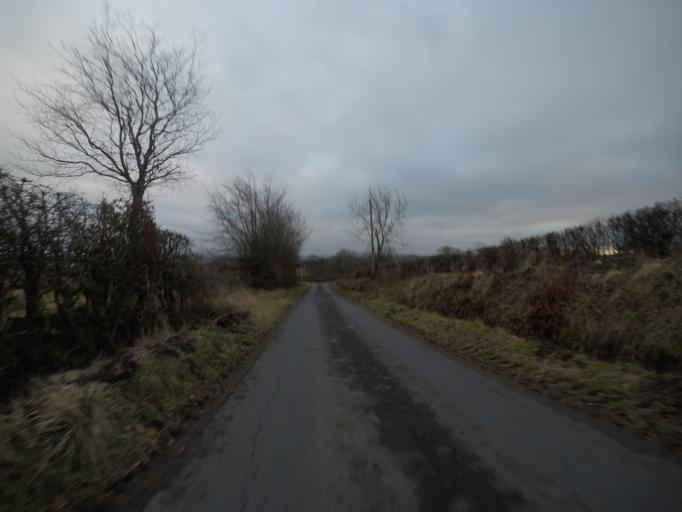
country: GB
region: Scotland
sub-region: North Ayrshire
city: Dalry
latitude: 55.7167
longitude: -4.7545
